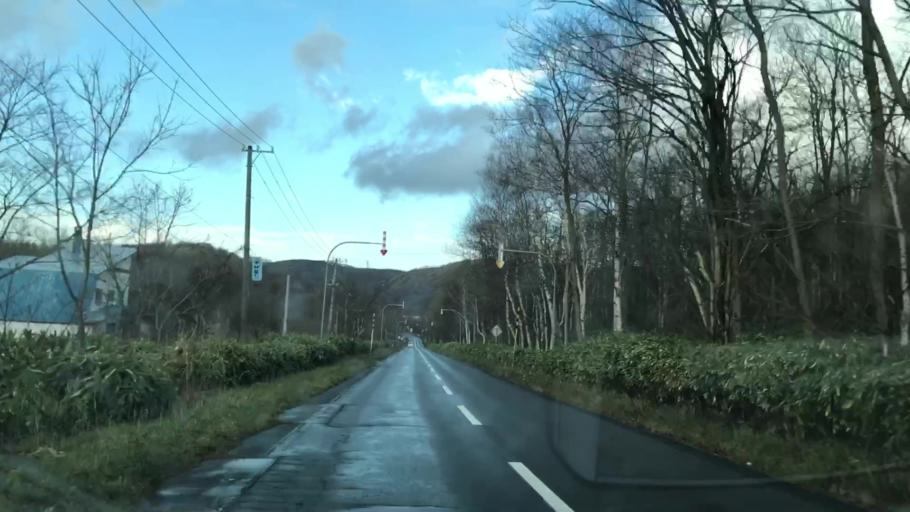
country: JP
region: Hokkaido
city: Yoichi
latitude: 43.3222
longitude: 140.5160
